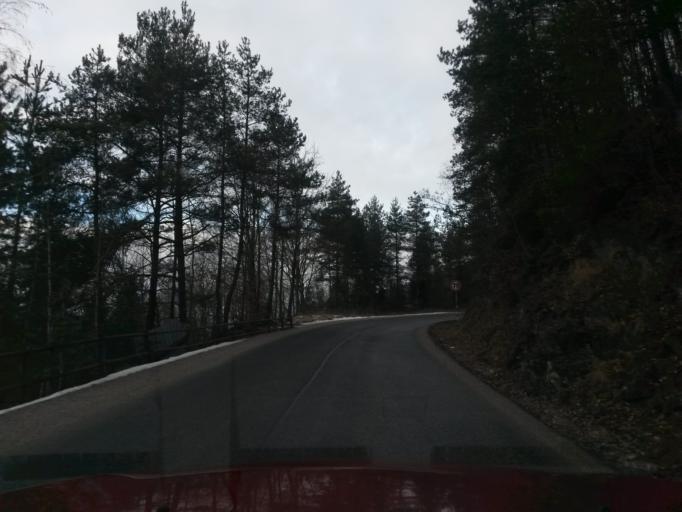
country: SK
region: Presovsky
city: Spisske Podhradie
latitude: 48.8766
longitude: 20.6868
